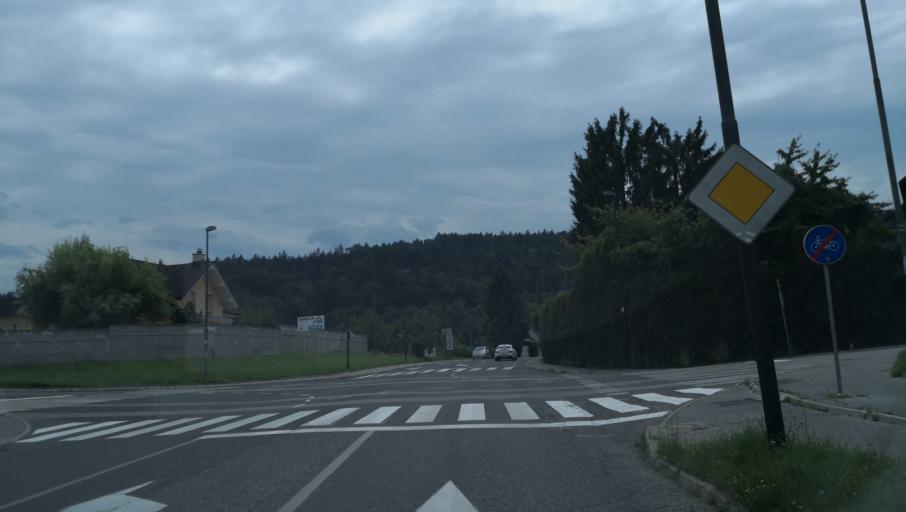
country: SI
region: Medvode
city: Zgornje Pirnice
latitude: 46.1020
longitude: 14.4616
